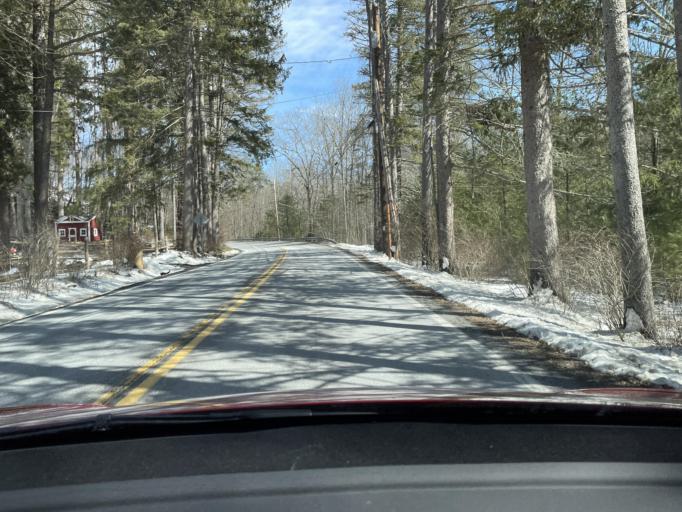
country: US
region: New York
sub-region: Ulster County
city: Shokan
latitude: 42.0628
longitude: -74.2494
